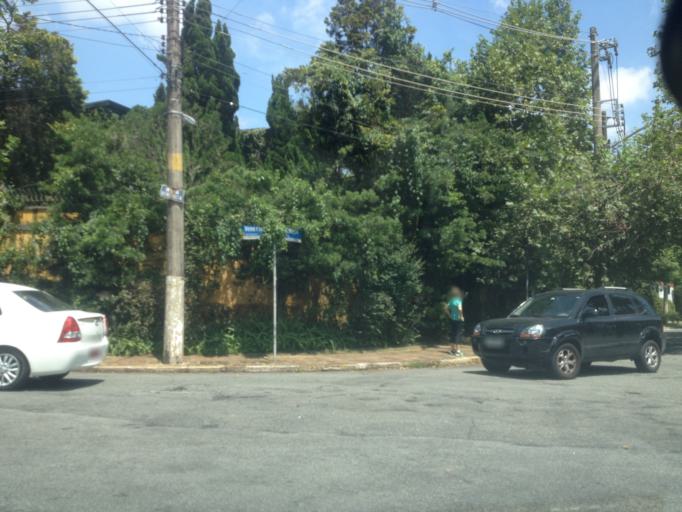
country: BR
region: Sao Paulo
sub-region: Sao Paulo
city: Sao Paulo
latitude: -23.5696
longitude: -46.6758
